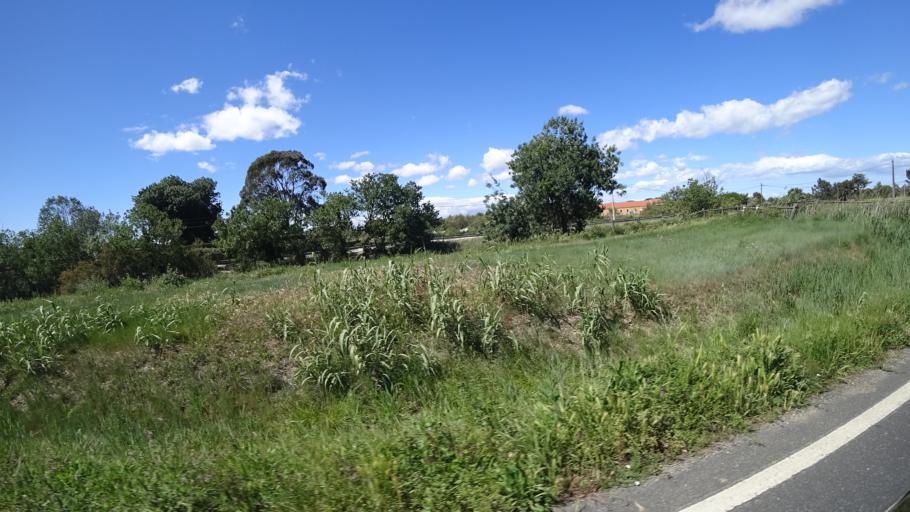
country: FR
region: Languedoc-Roussillon
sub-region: Departement des Pyrenees-Orientales
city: Saint-Nazaire
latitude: 42.6723
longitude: 2.9848
